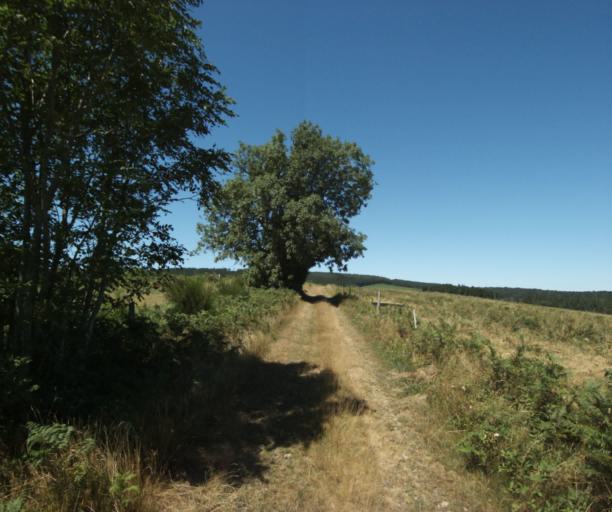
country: FR
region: Midi-Pyrenees
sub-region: Departement du Tarn
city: Dourgne
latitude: 43.4363
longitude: 2.1547
